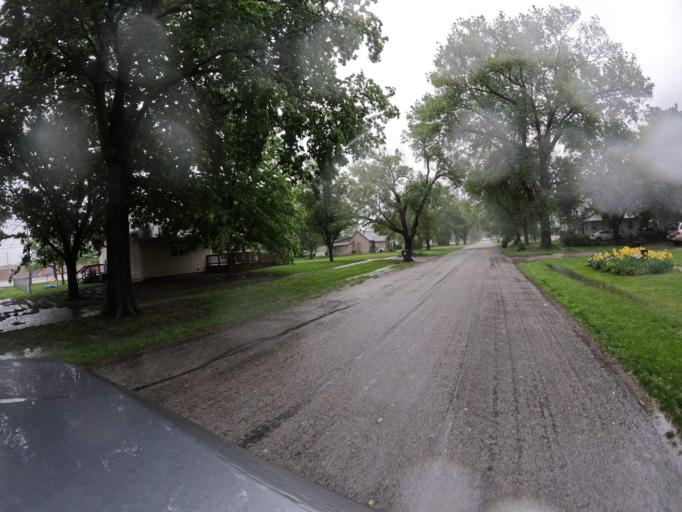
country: US
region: Nebraska
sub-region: Gage County
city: Wymore
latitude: 40.1386
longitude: -96.6659
